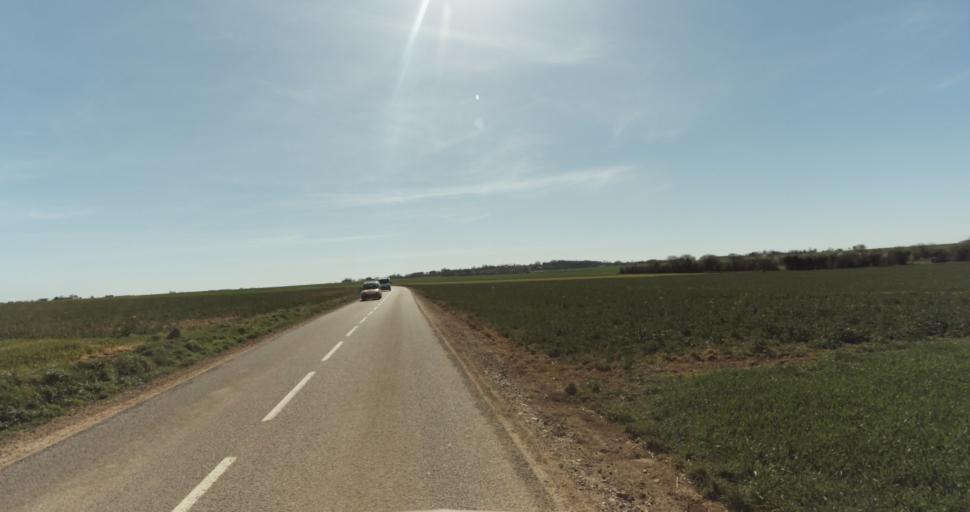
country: FR
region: Lower Normandy
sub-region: Departement du Calvados
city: Canon
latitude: 49.0450
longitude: -0.0674
